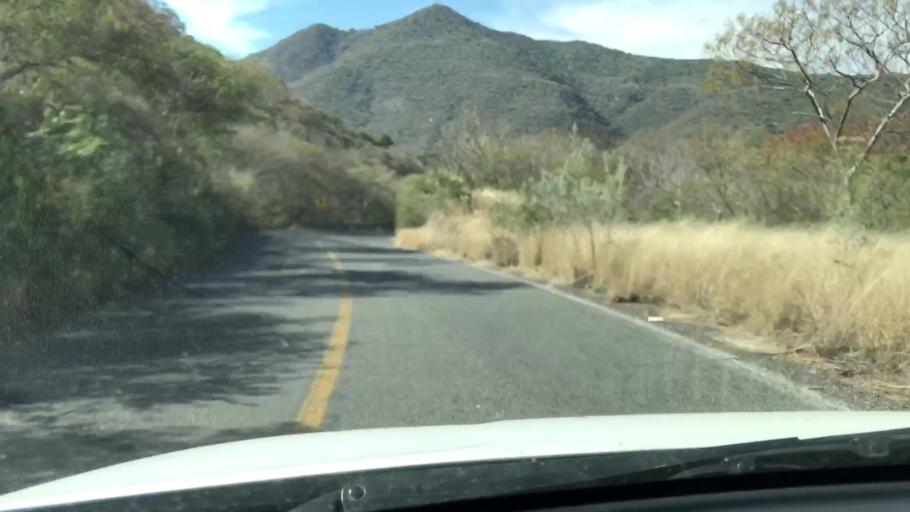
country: MX
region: Jalisco
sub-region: Zacoalco de Torres
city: Barranca de Otates (Barranca de Otatan)
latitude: 20.2569
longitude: -103.6753
